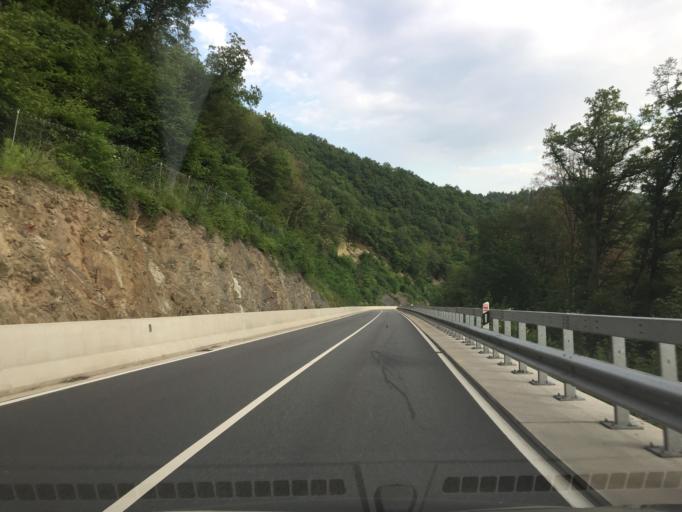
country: DE
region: Rheinland-Pfalz
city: Bendorf
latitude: 50.4432
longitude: 7.5810
